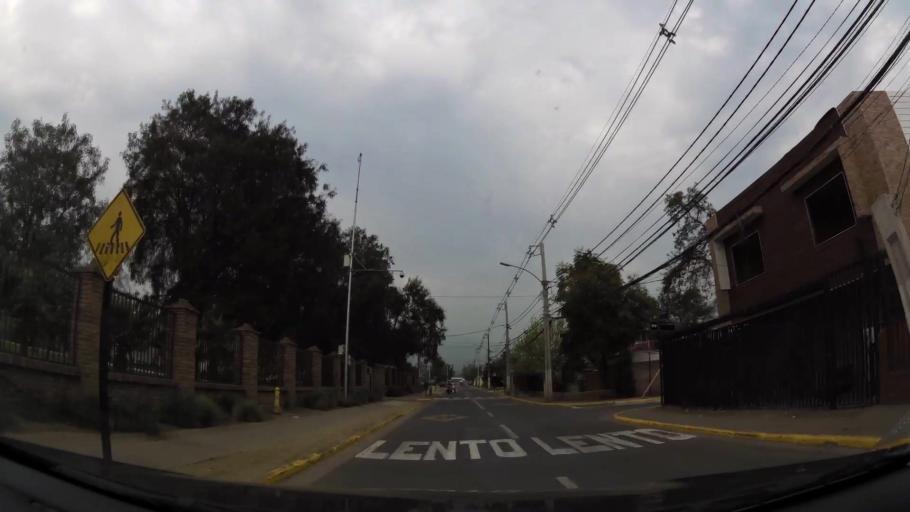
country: CL
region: Santiago Metropolitan
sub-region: Provincia de Chacabuco
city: Chicureo Abajo
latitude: -33.2063
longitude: -70.6719
